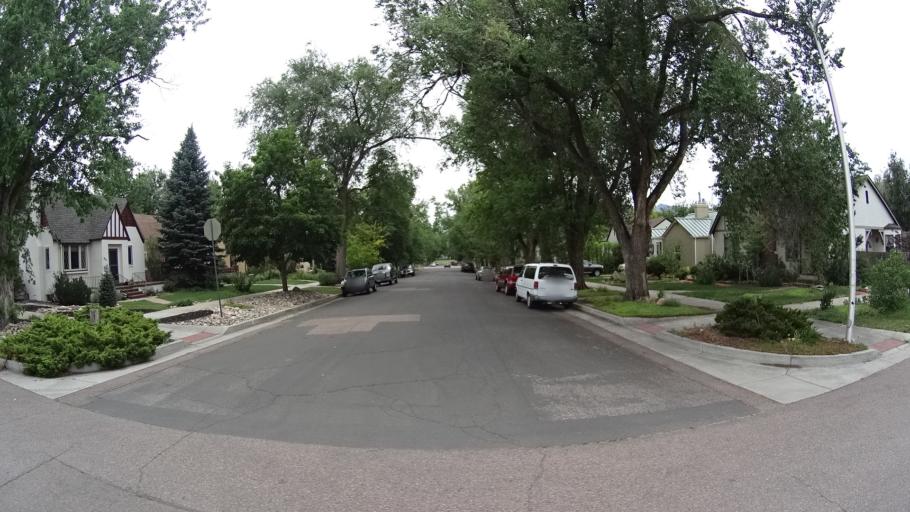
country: US
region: Colorado
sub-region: El Paso County
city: Colorado Springs
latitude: 38.8431
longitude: -104.8018
